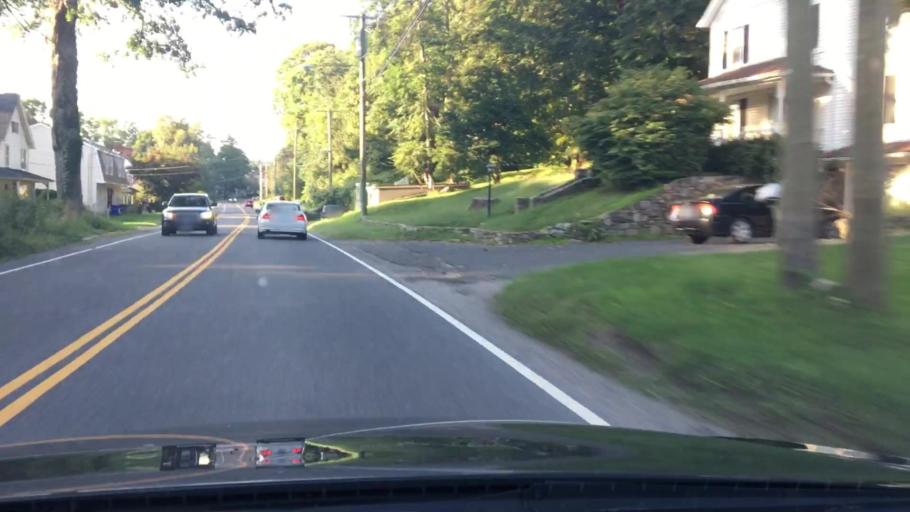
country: US
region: Connecticut
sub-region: Litchfield County
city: New Milford
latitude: 41.5683
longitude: -73.4059
